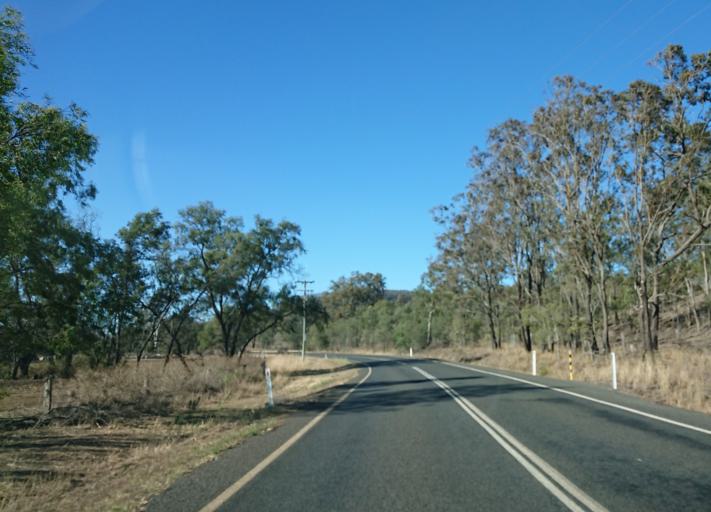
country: AU
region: Queensland
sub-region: Toowoomba
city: Top Camp
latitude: -27.7330
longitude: 152.1091
